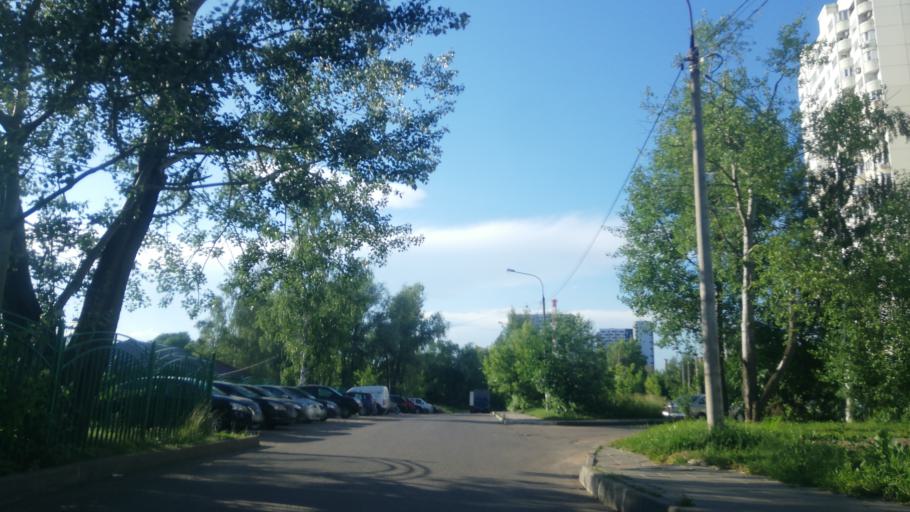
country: RU
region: Moskovskaya
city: Dolgoprudnyy
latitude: 55.9414
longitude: 37.4852
